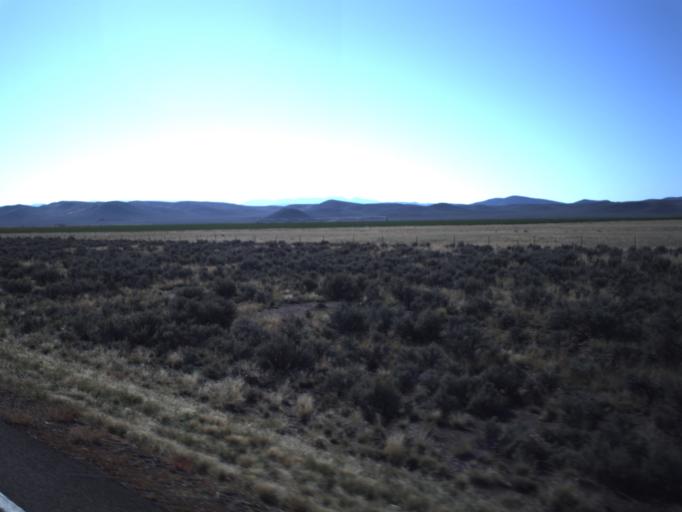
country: US
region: Utah
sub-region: Washington County
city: Enterprise
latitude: 37.7642
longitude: -113.8111
